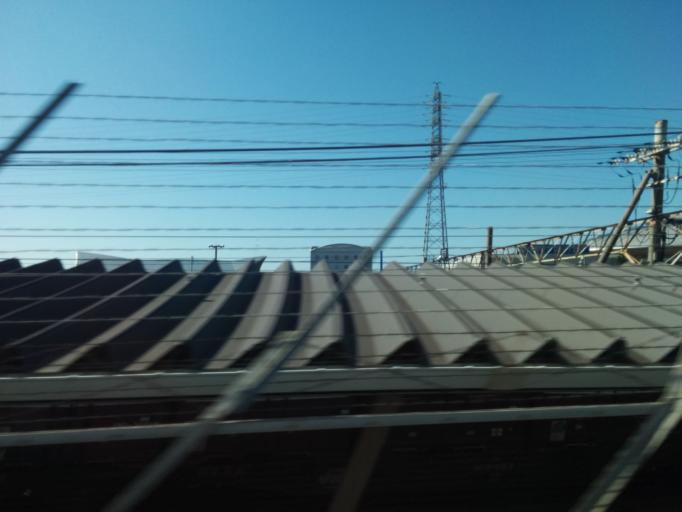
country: JP
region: Aichi
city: Nagoya-shi
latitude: 35.0952
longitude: 136.9268
